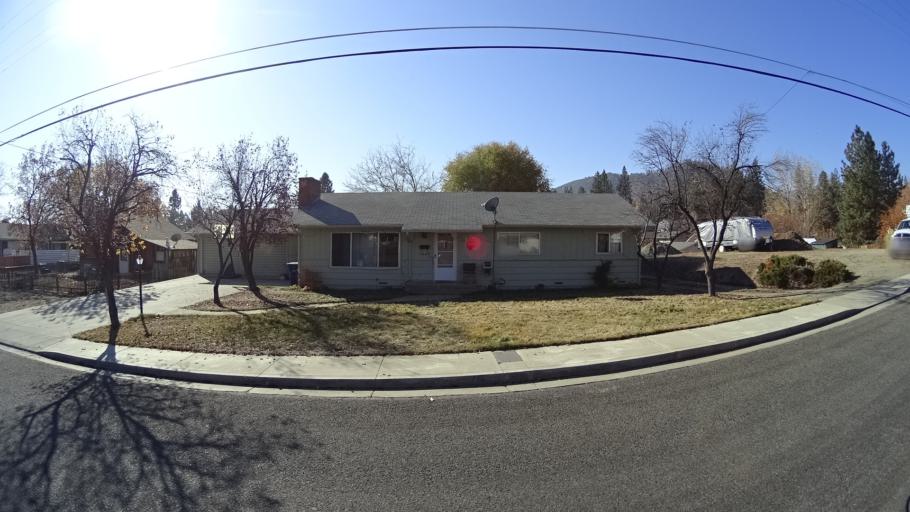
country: US
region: California
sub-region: Siskiyou County
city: Yreka
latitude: 41.7361
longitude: -122.6515
